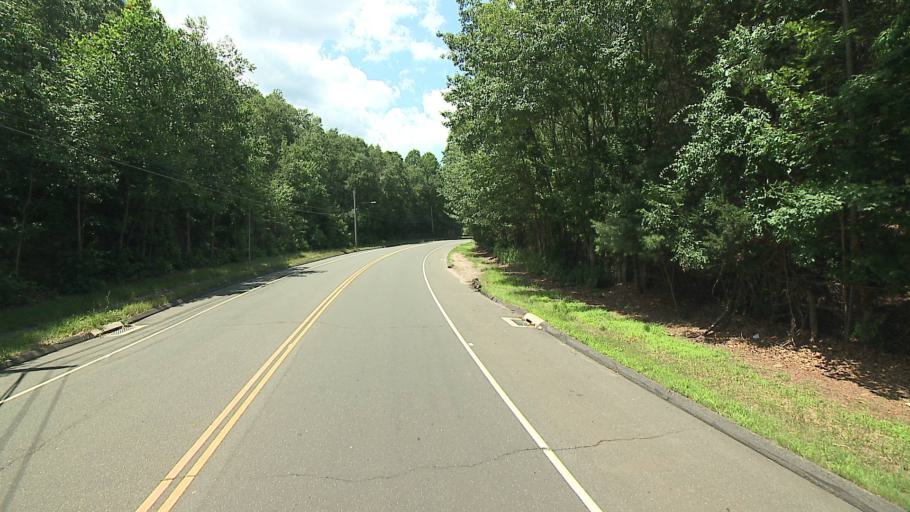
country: US
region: Connecticut
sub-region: Fairfield County
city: Trumbull
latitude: 41.2515
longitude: -73.1984
